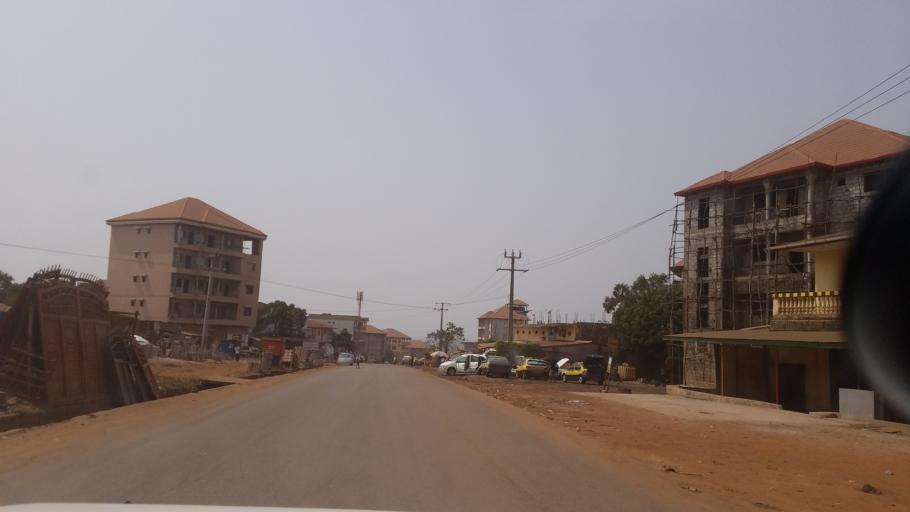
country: GN
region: Kindia
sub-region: Prefecture de Dubreka
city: Dubreka
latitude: 9.6707
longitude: -13.5604
